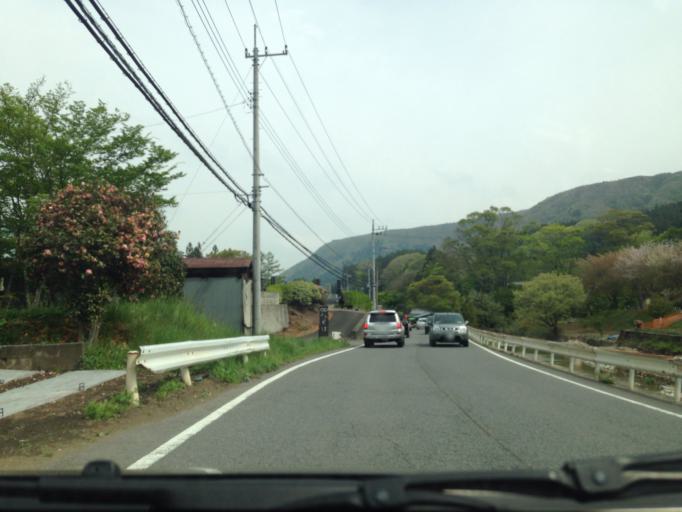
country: JP
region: Tochigi
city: Yaita
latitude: 36.9827
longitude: 139.7859
